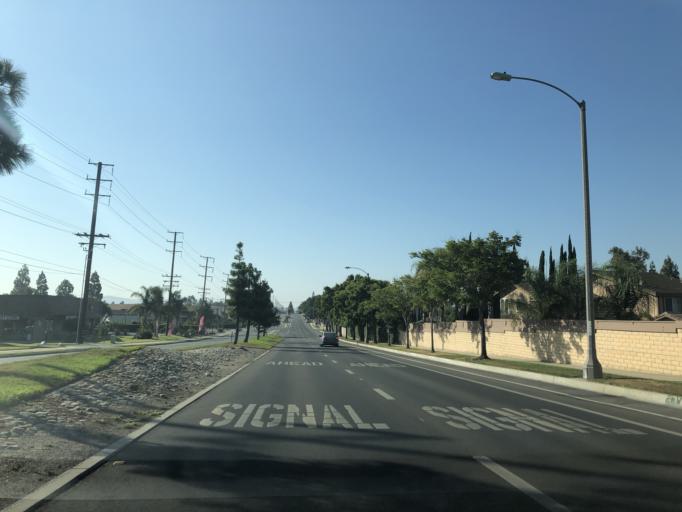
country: US
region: California
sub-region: Riverside County
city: Corona
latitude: 33.9095
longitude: -117.5838
